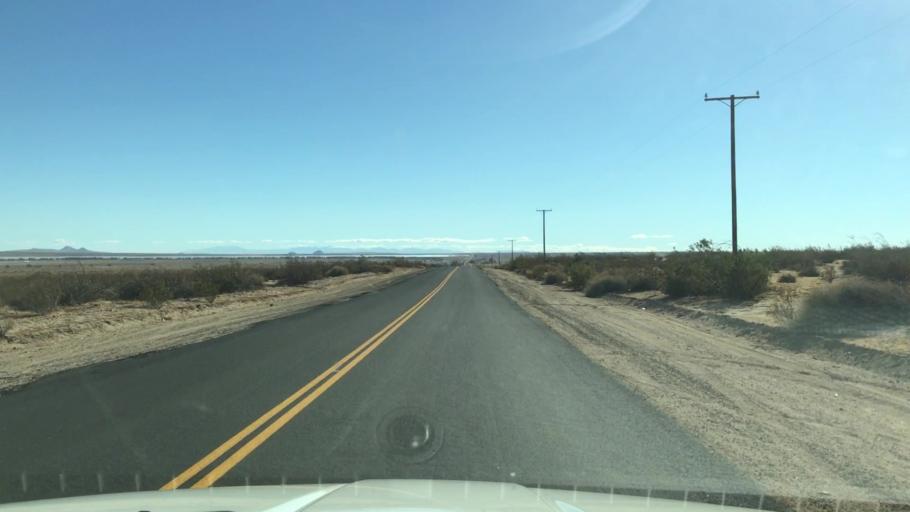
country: US
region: California
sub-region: Kern County
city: California City
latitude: 35.3070
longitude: -117.9860
